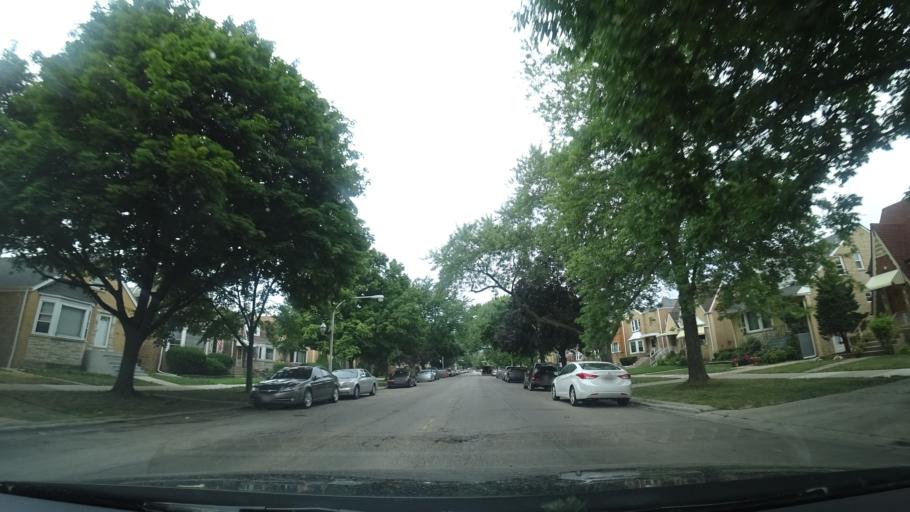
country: US
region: Illinois
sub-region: Cook County
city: Harwood Heights
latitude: 41.9625
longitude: -87.7630
